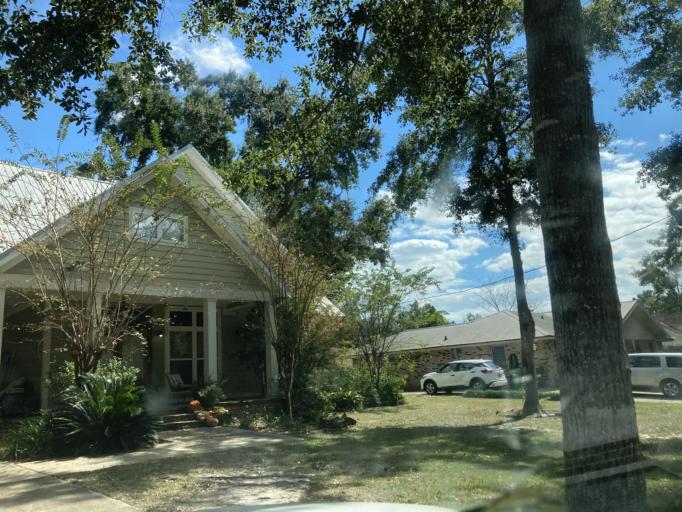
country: US
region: Mississippi
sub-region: Jackson County
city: Gulf Hills
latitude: 30.4462
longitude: -88.8435
